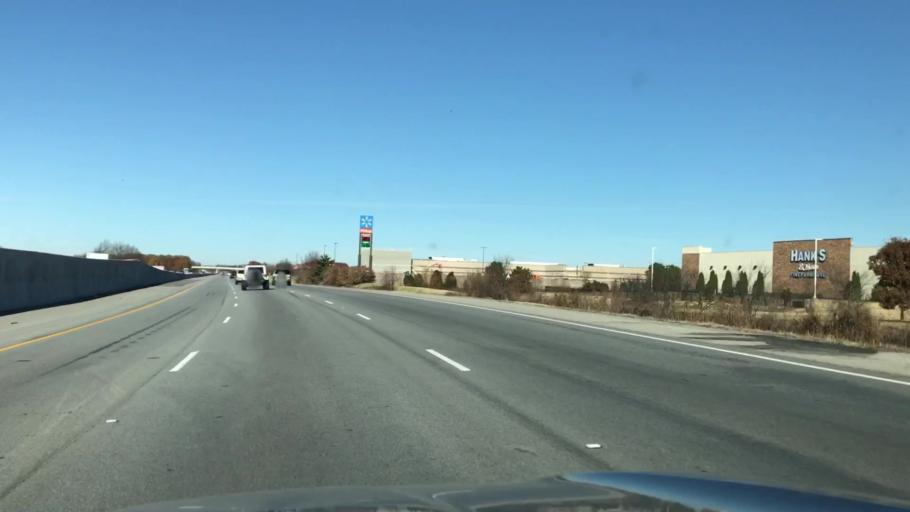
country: US
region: Arkansas
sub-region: Benton County
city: Lowell
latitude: 36.2758
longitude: -94.1509
